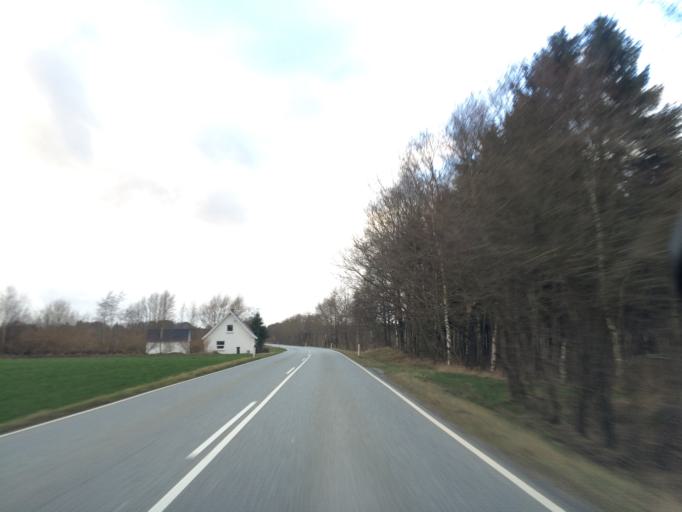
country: DK
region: Central Jutland
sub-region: Silkeborg Kommune
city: Virklund
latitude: 56.1035
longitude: 9.5917
